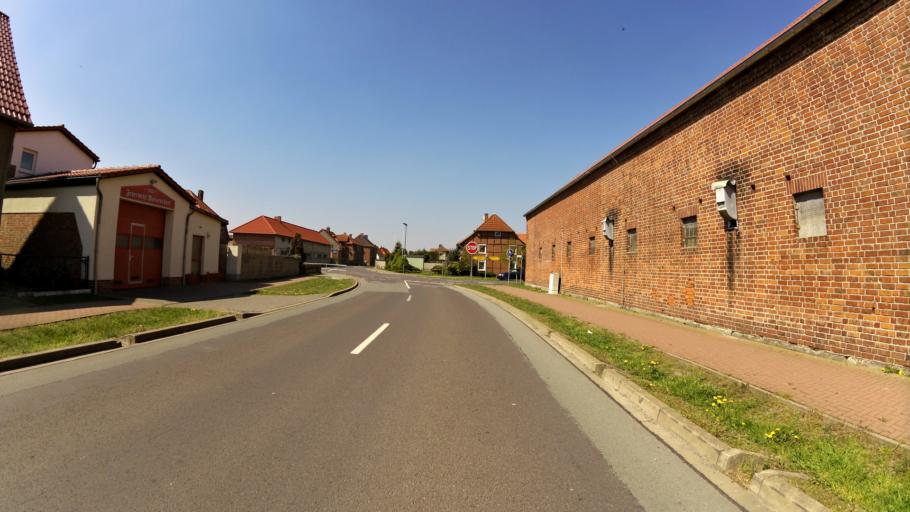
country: DE
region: Saxony-Anhalt
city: Oebisfelde
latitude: 52.4488
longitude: 10.9981
